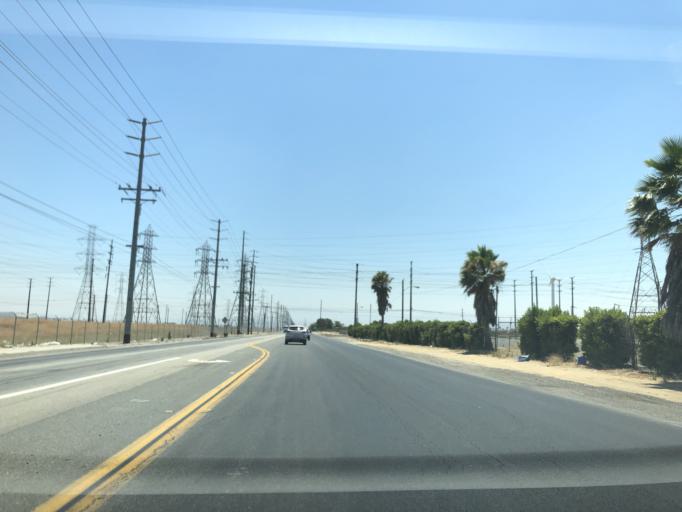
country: US
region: California
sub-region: San Bernardino County
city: Rancho Cucamonga
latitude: 34.0898
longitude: -117.5239
